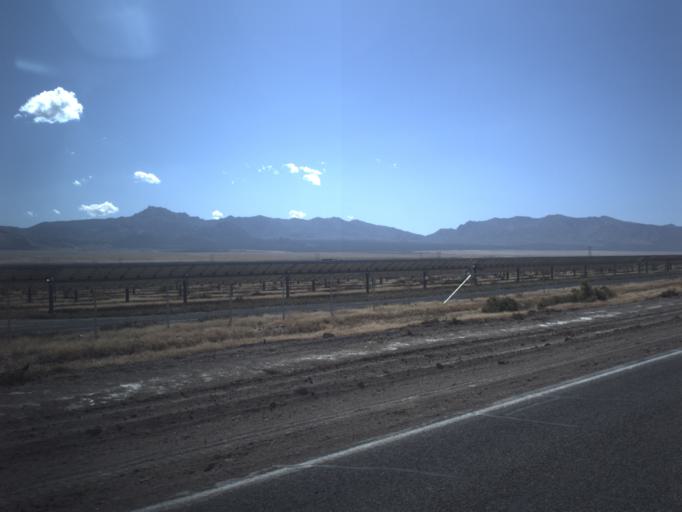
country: US
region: Utah
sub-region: Beaver County
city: Milford
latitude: 38.5040
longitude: -112.9912
